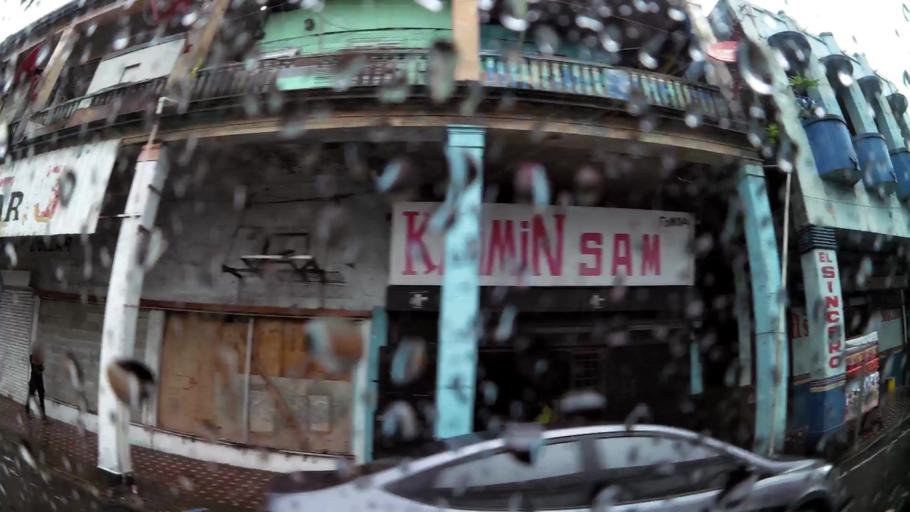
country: PA
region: Colon
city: Colon
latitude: 9.3583
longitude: -79.9041
